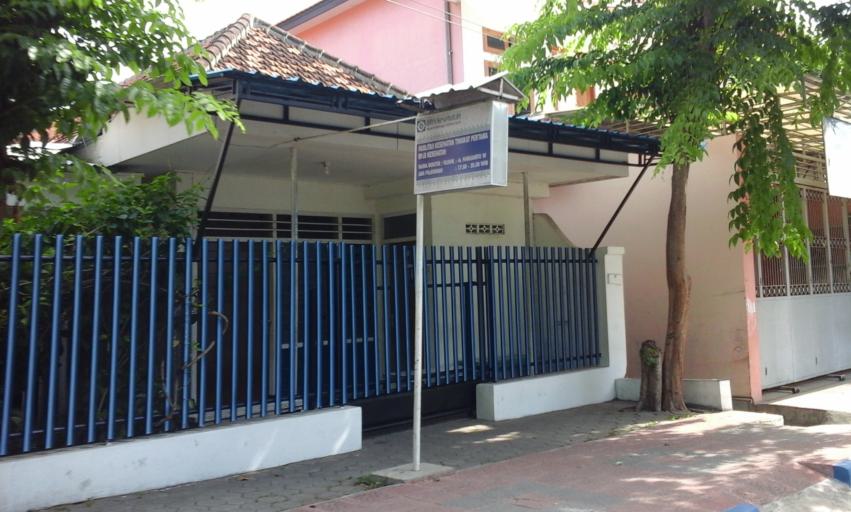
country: ID
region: East Java
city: Banyuwangi
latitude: -8.2163
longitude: 114.3643
